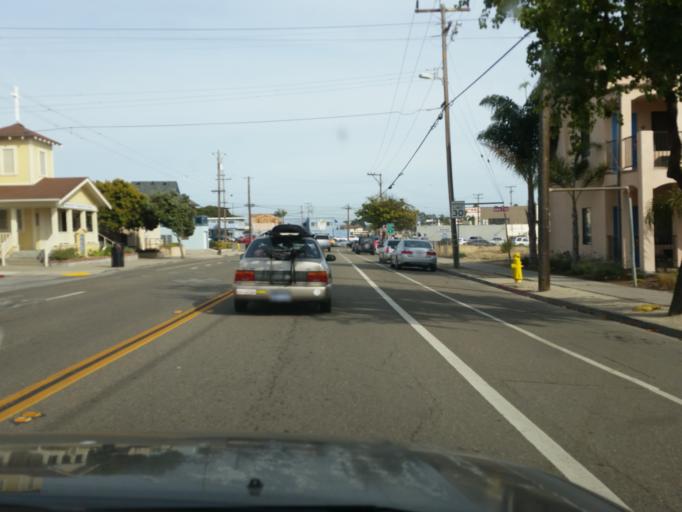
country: US
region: California
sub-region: San Luis Obispo County
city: Pismo Beach
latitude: 35.1427
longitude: -120.6432
